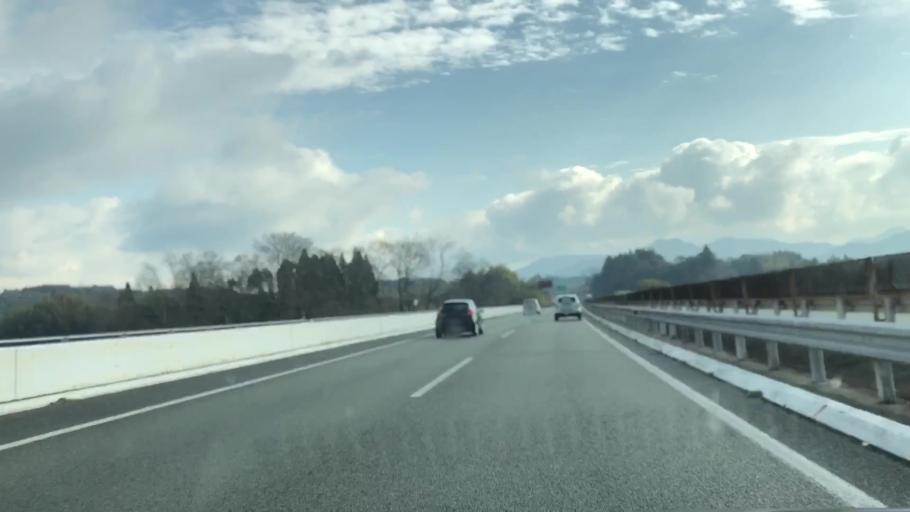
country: JP
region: Kumamoto
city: Tamana
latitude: 32.9924
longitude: 130.6016
